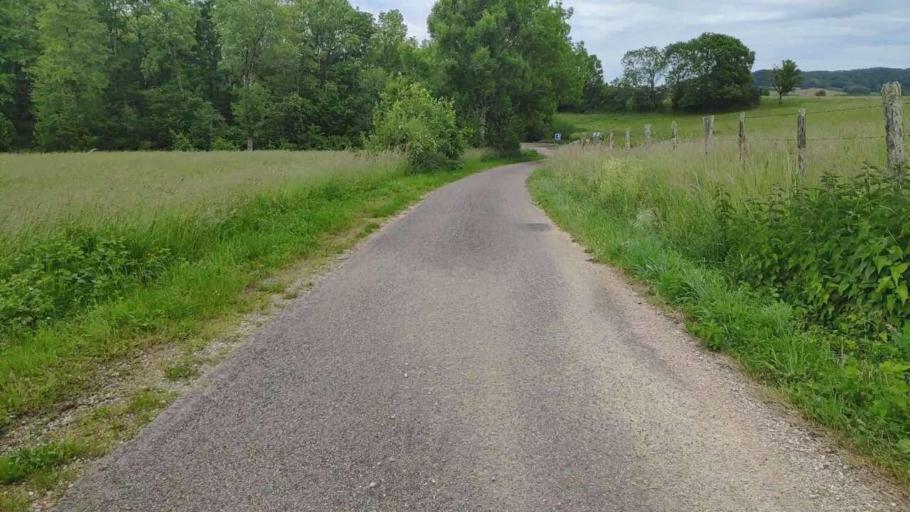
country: FR
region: Franche-Comte
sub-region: Departement du Jura
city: Perrigny
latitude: 46.7571
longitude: 5.5725
